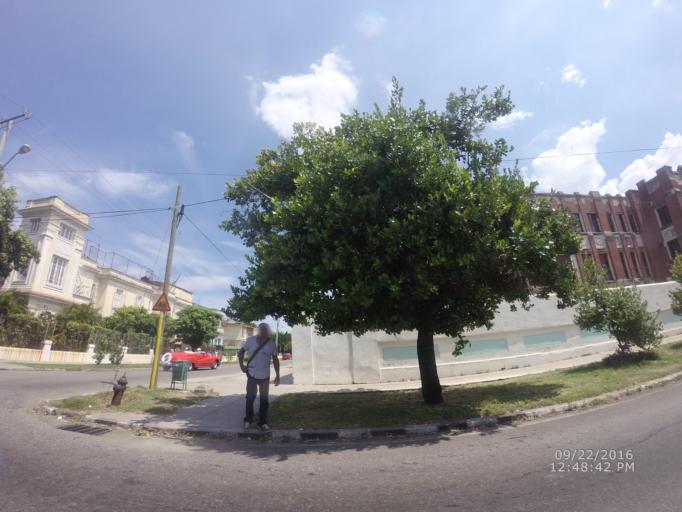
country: CU
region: La Habana
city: Havana
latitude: 23.1324
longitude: -82.3950
